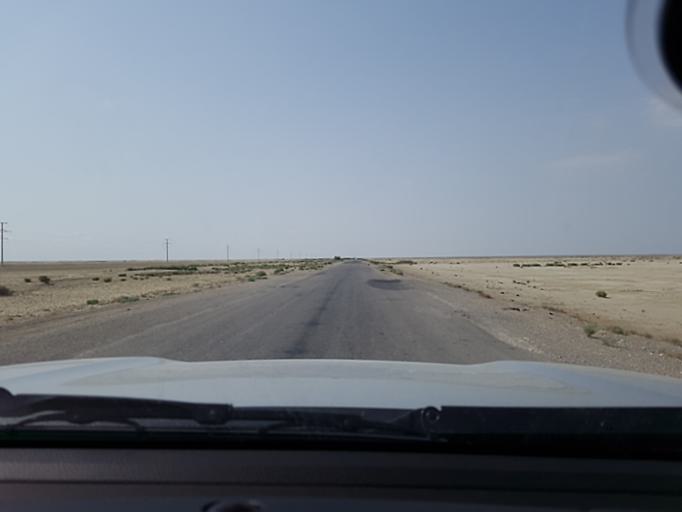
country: TM
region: Balkan
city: Gumdag
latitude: 38.9861
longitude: 54.5872
